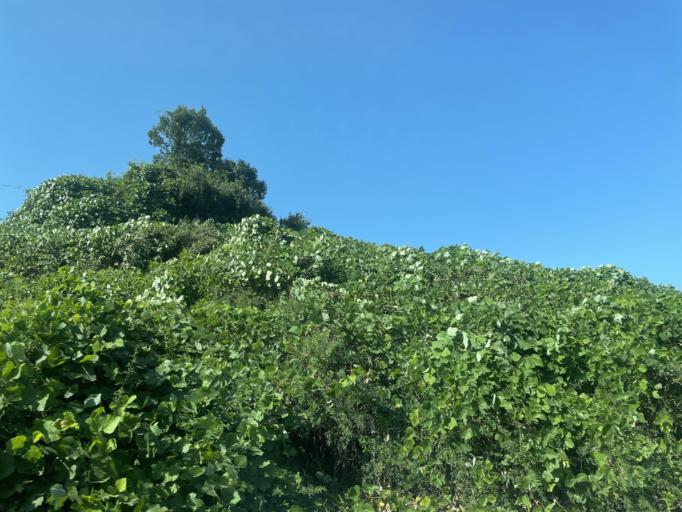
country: JP
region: Nara
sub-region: Ikoma-shi
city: Ikoma
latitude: 34.7262
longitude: 135.7451
